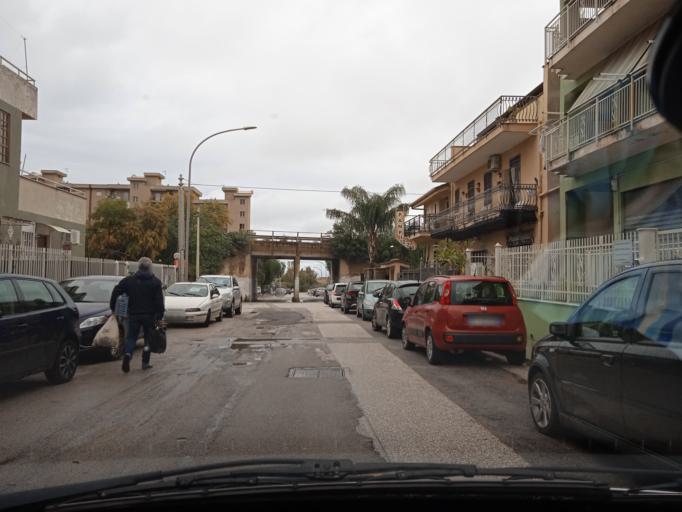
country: IT
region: Sicily
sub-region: Palermo
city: Villabate
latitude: 38.0799
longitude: 13.4443
